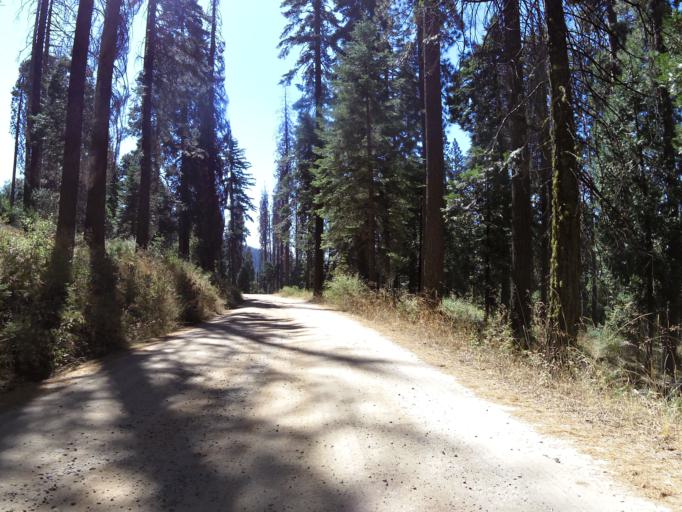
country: US
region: California
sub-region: Madera County
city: Oakhurst
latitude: 37.4172
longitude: -119.5908
